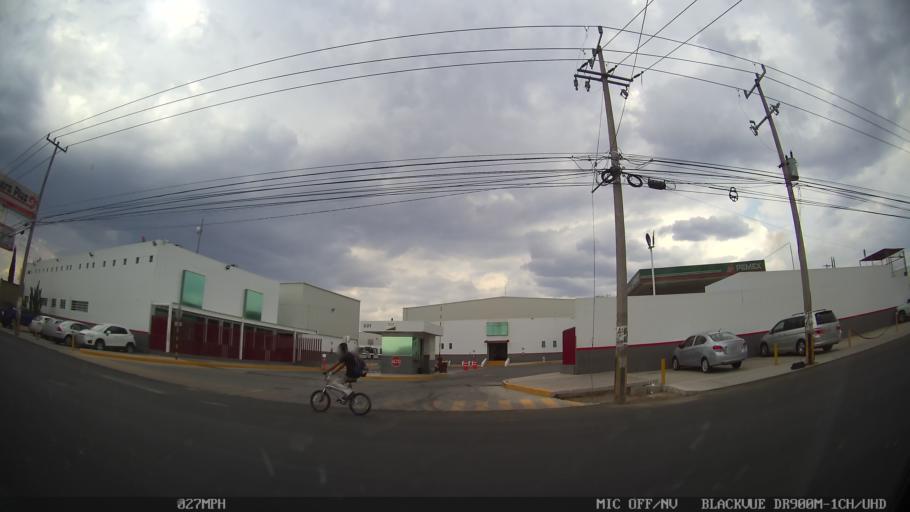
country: MX
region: Jalisco
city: Tlaquepaque
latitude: 20.6208
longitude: -103.2815
